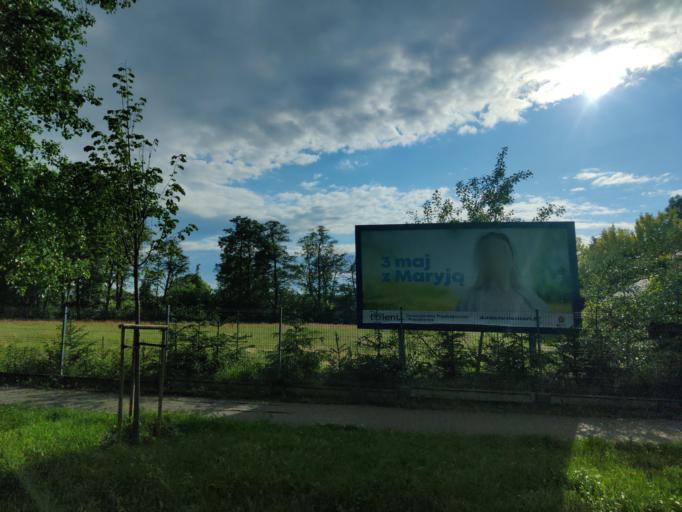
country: PL
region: Masovian Voivodeship
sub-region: Warszawa
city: Kabaty
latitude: 52.1232
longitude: 21.1029
